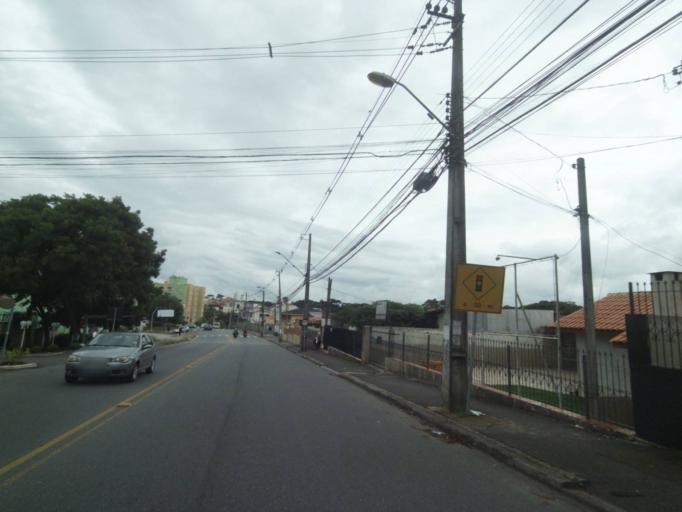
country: BR
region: Parana
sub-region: Curitiba
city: Curitiba
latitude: -25.4607
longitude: -49.3365
